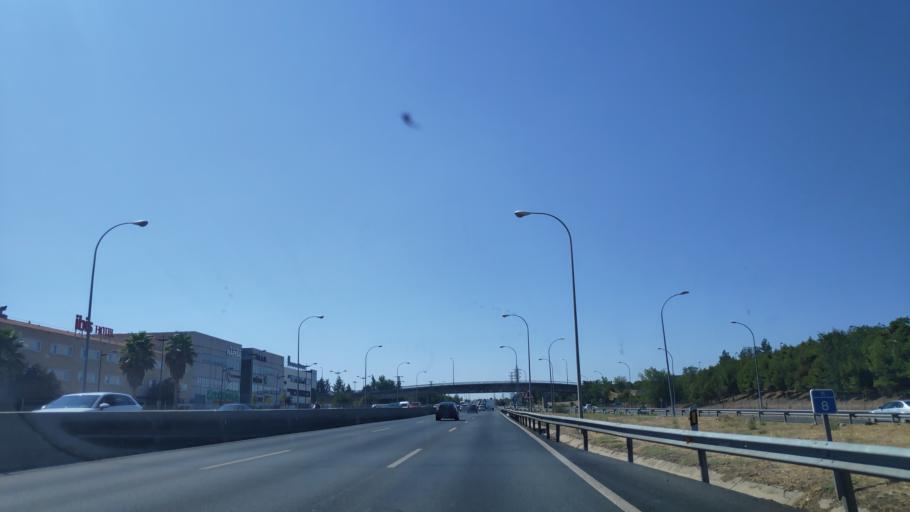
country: ES
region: Madrid
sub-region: Provincia de Madrid
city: Getafe
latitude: 40.3172
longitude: -3.7354
